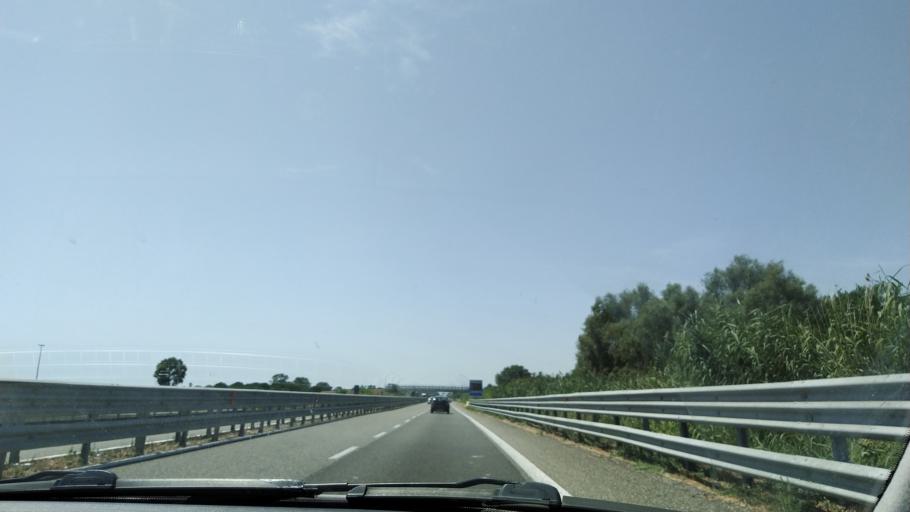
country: IT
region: Basilicate
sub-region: Provincia di Matera
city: Marconia
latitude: 40.3445
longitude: 16.7639
